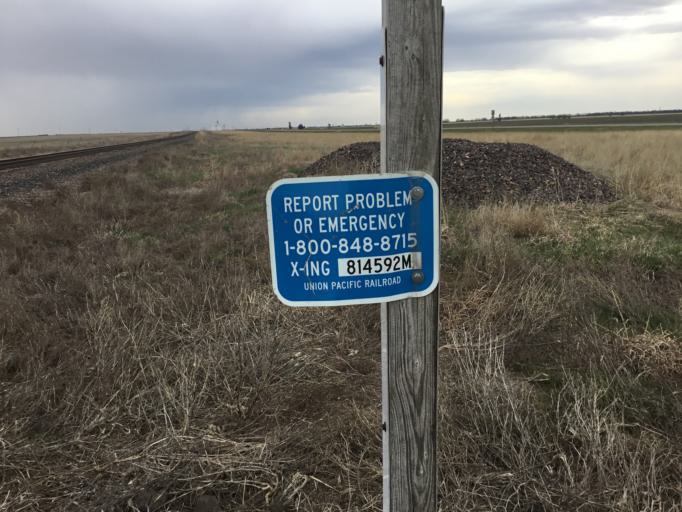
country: US
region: Kansas
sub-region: Russell County
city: Russell
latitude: 38.8826
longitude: -98.9281
